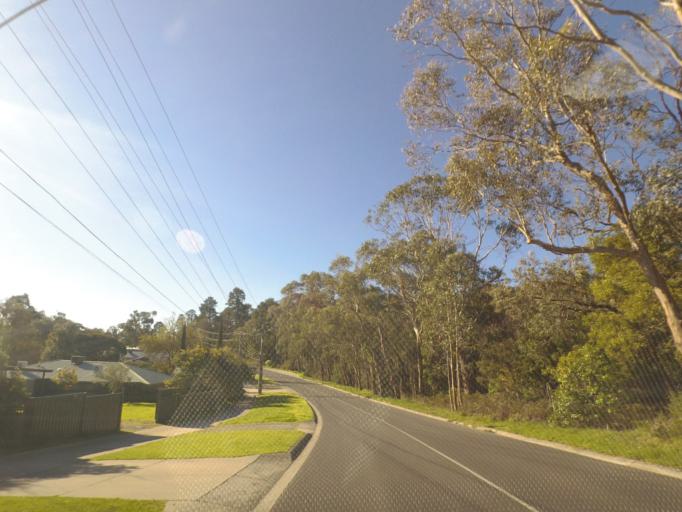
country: AU
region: Victoria
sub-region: Yarra Ranges
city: Montrose
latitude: -37.8035
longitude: 145.3396
